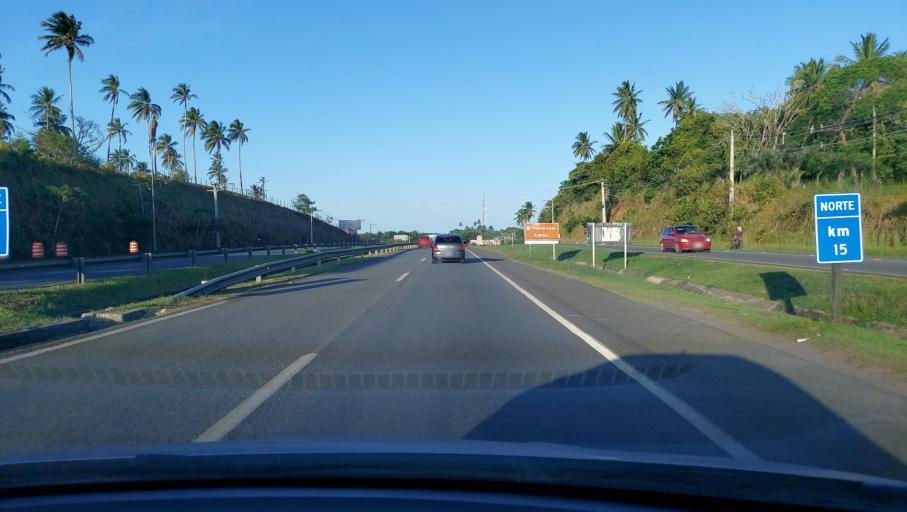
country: BR
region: Bahia
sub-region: Lauro De Freitas
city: Lauro de Freitas
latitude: -12.8177
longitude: -38.2458
